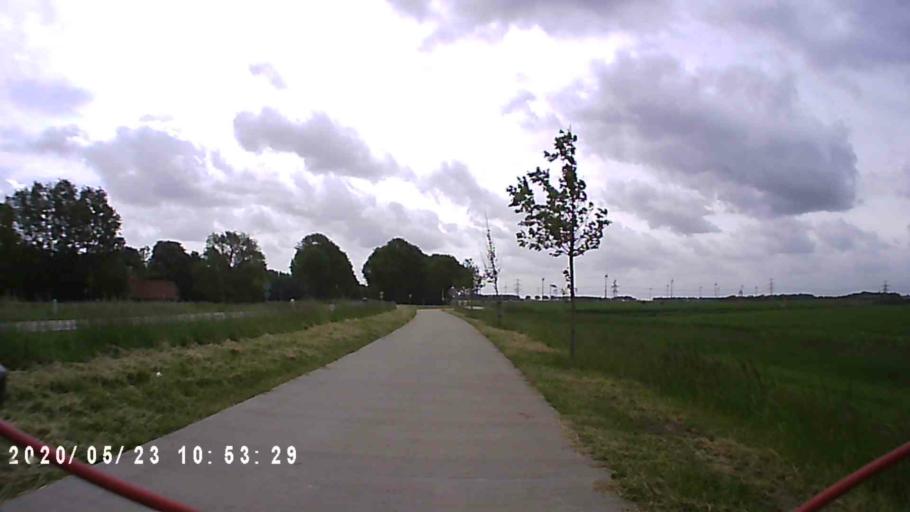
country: NL
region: Groningen
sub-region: Gemeente Delfzijl
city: Delfzijl
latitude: 53.3107
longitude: 6.9435
